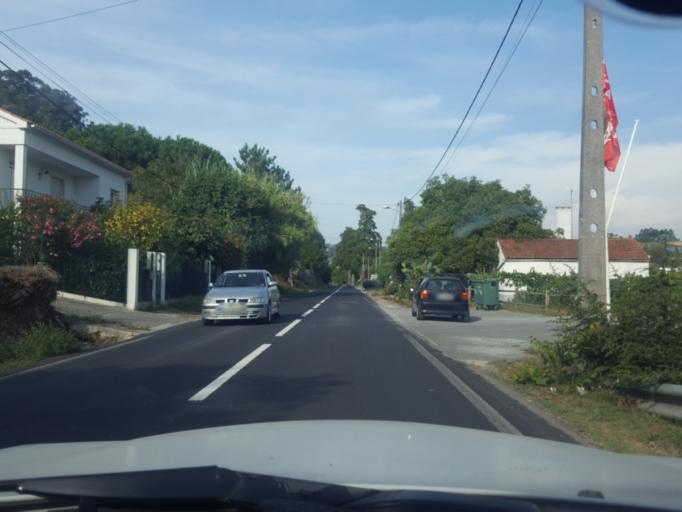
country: PT
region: Leiria
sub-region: Leiria
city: Leiria
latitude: 39.7101
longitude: -8.7915
